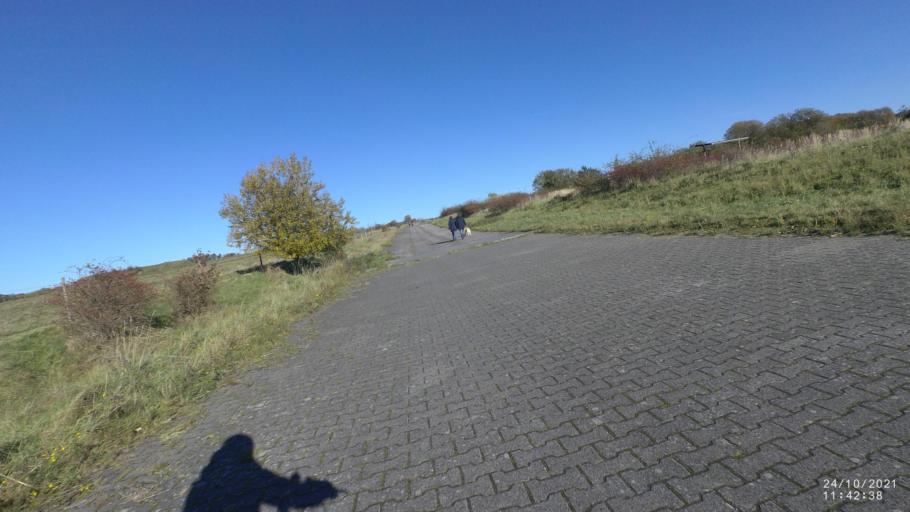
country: DE
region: North Rhine-Westphalia
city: Hemer
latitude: 51.3851
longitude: 7.7940
